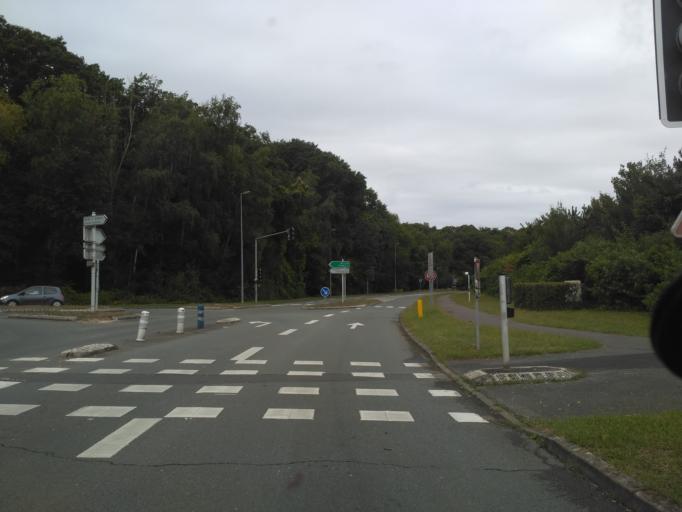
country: FR
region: Ile-de-France
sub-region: Departement de Seine-et-Marne
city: Cesson
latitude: 48.5600
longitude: 2.6156
